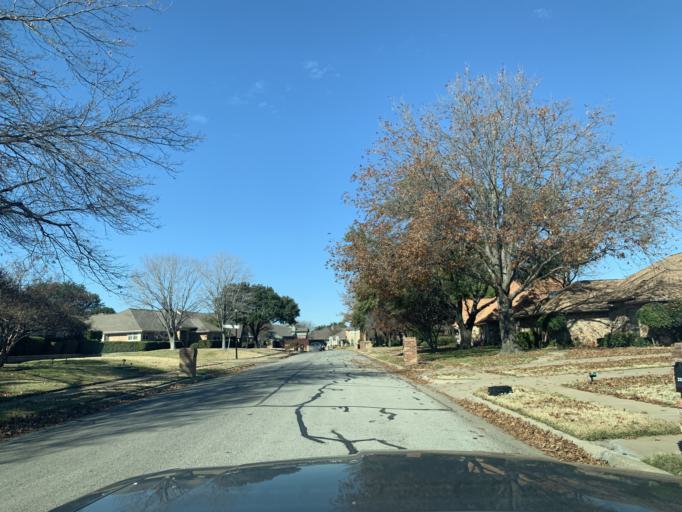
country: US
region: Texas
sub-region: Tarrant County
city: Bedford
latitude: 32.8450
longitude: -97.1536
